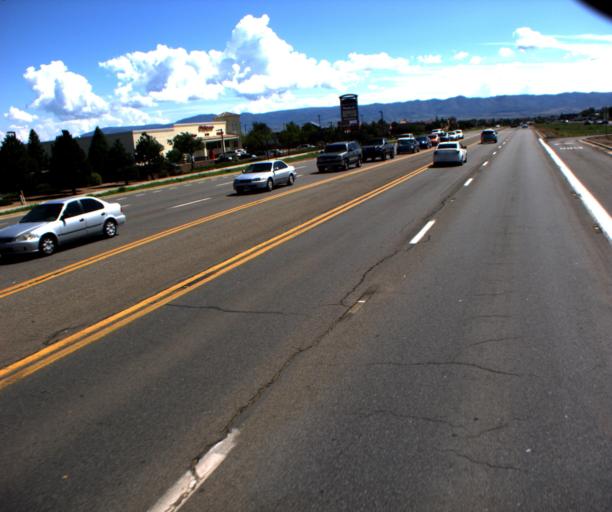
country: US
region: Arizona
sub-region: Yavapai County
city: Prescott Valley
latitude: 34.5833
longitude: -112.3409
